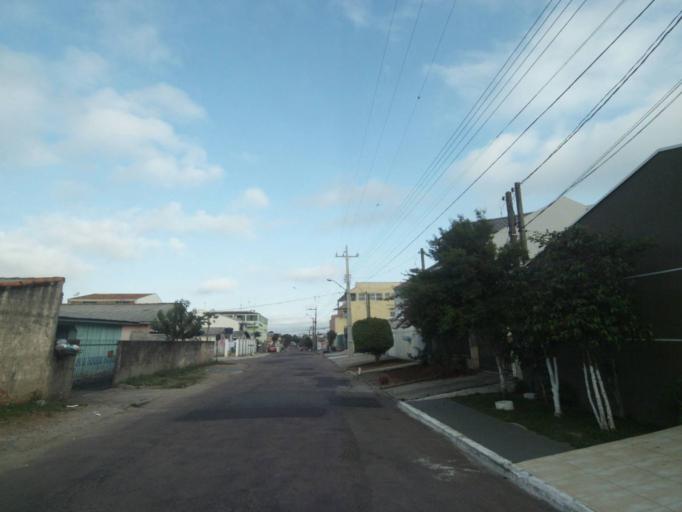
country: BR
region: Parana
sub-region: Sao Jose Dos Pinhais
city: Sao Jose dos Pinhais
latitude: -25.5470
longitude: -49.2602
